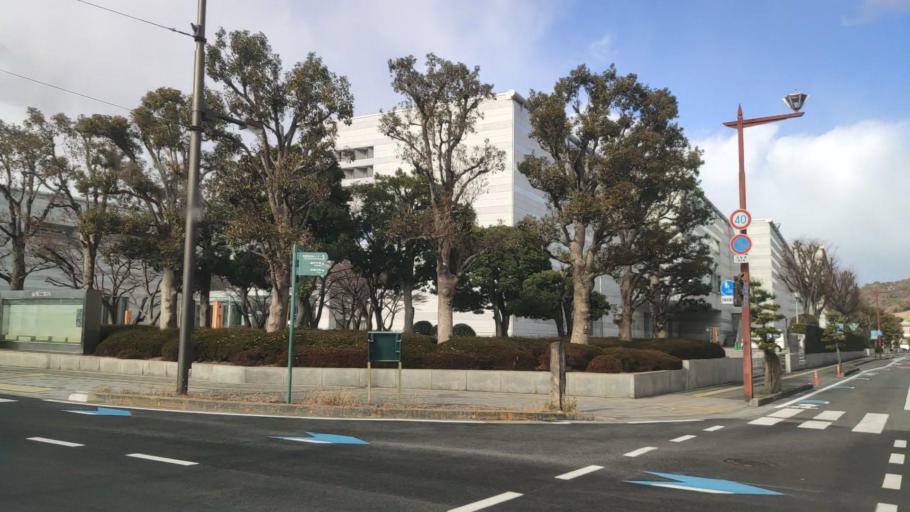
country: JP
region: Ehime
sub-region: Shikoku-chuo Shi
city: Matsuyama
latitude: 33.8475
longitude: 132.7805
